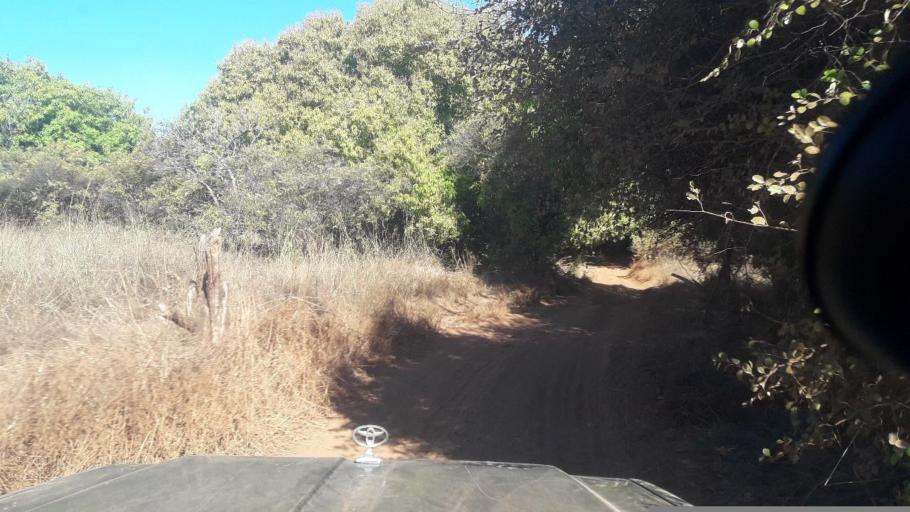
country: MG
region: Boeny
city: Sitampiky
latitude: -16.3267
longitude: 45.6331
